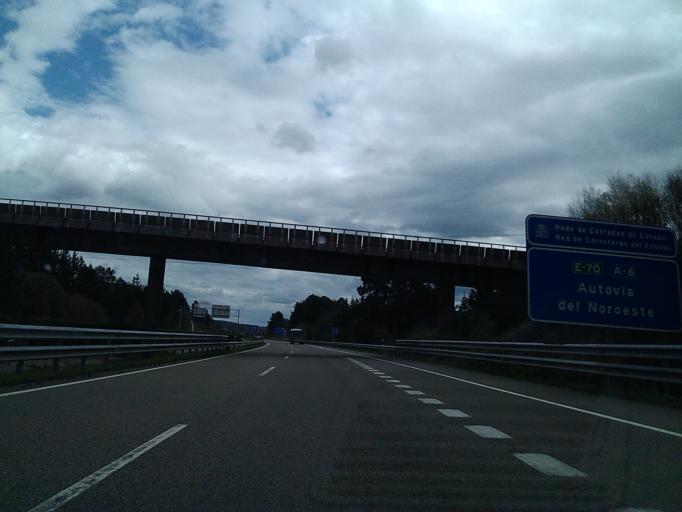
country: ES
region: Galicia
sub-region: Provincia de Lugo
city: Guitiriz
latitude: 43.1925
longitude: -7.9489
